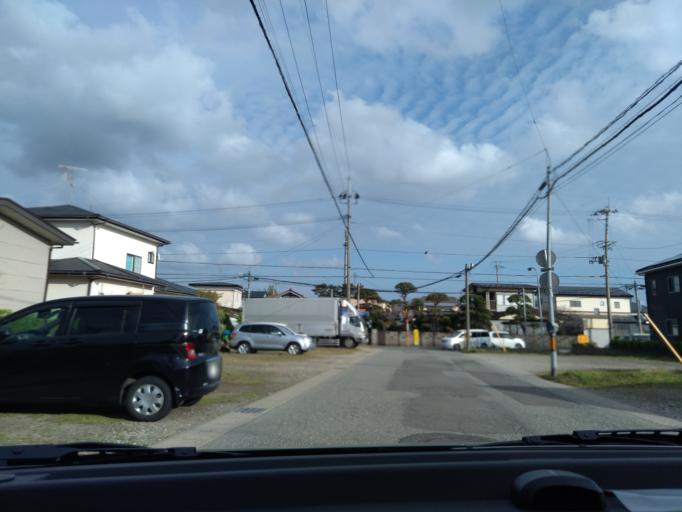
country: JP
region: Akita
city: Akita Shi
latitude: 39.7693
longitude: 140.0829
